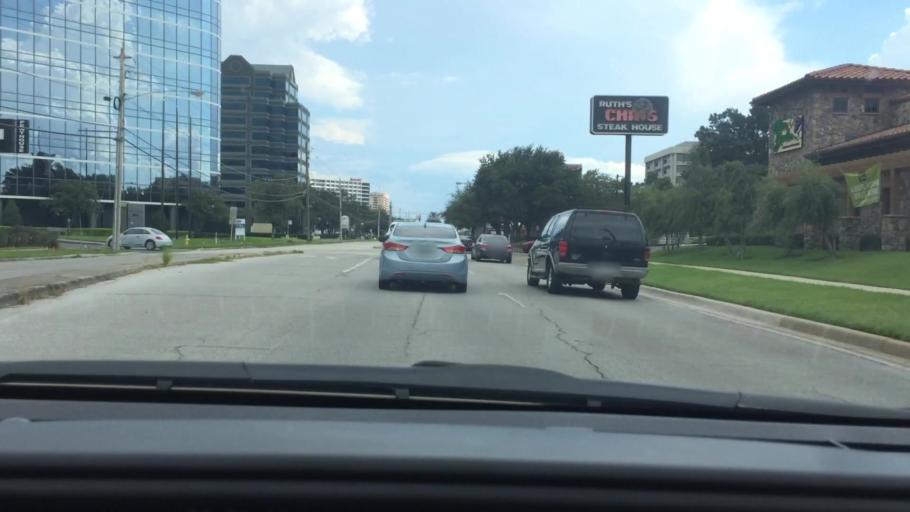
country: US
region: Florida
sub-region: Hillsborough County
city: Egypt Lake-Leto
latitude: 27.9583
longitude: -82.5242
